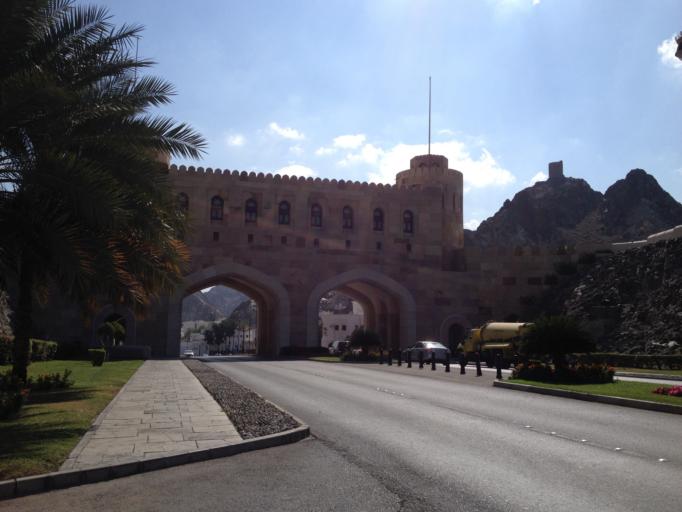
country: OM
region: Muhafazat Masqat
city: Muscat
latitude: 23.6184
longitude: 58.5866
